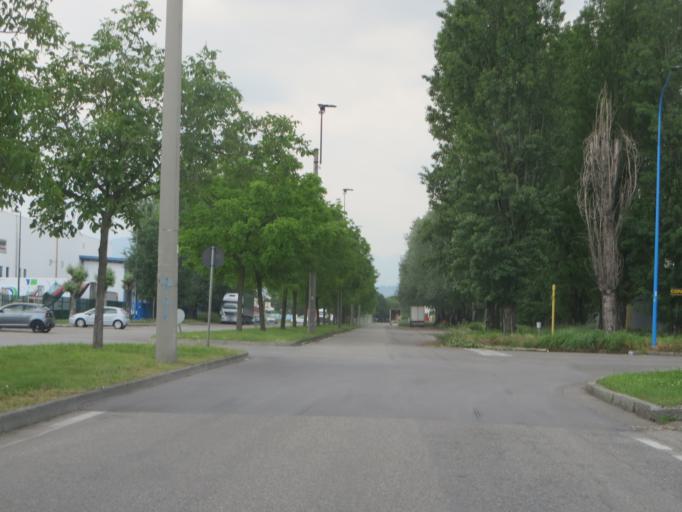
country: IT
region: Lombardy
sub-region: Provincia di Brescia
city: Roncadelle
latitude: 45.5145
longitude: 10.1572
